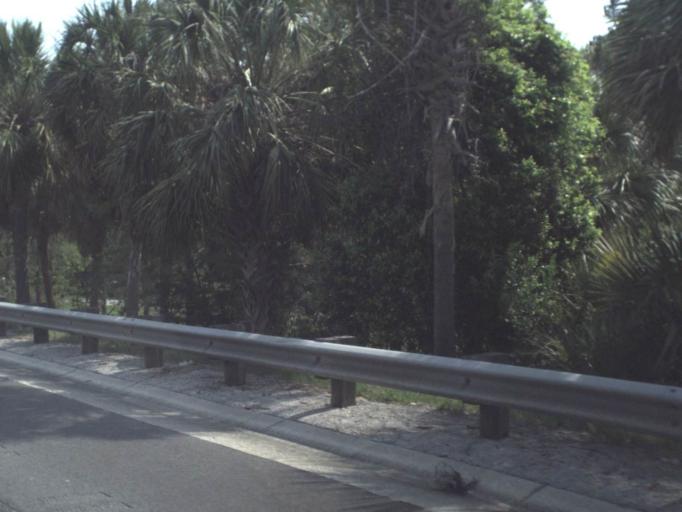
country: US
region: Florida
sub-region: Nassau County
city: Yulee
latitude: 30.5181
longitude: -81.6350
